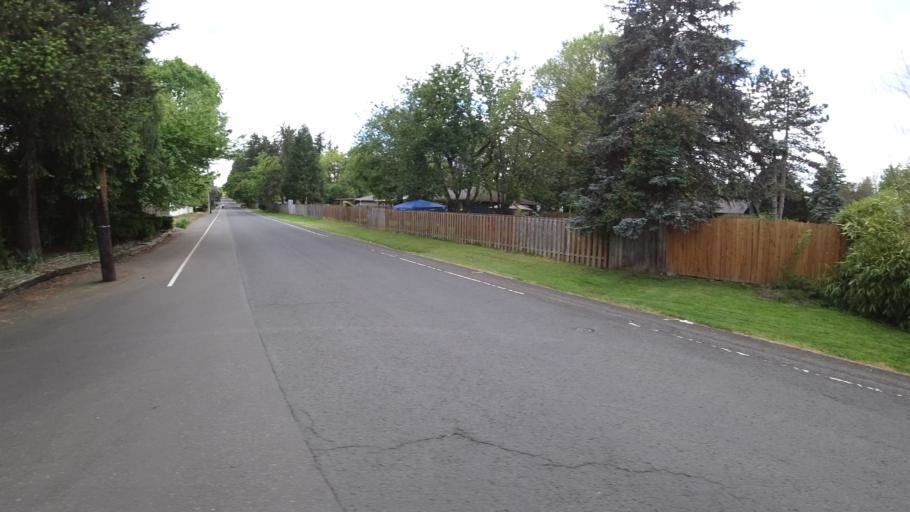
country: US
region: Oregon
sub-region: Washington County
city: Beaverton
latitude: 45.4803
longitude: -122.8216
